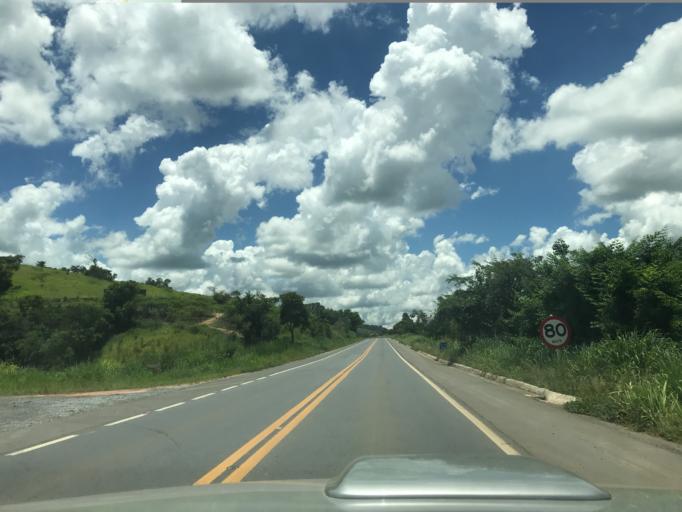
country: BR
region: Minas Gerais
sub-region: Perdoes
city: Perdoes
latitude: -21.0932
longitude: -45.1003
